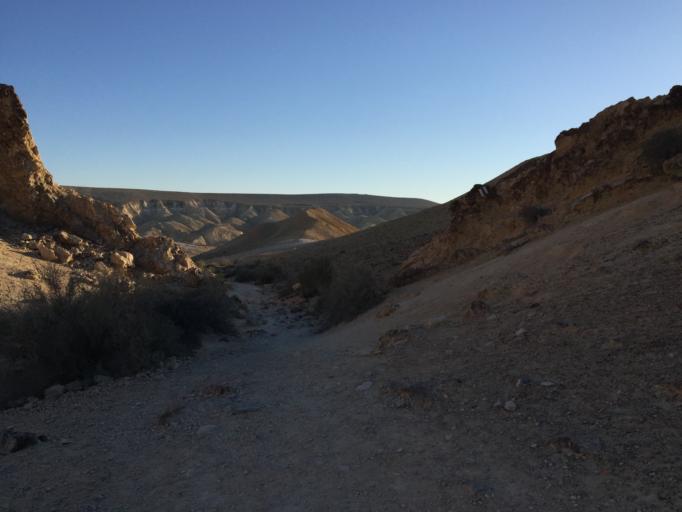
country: IL
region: Southern District
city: Midreshet Ben-Gurion
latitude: 30.8459
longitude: 34.7560
